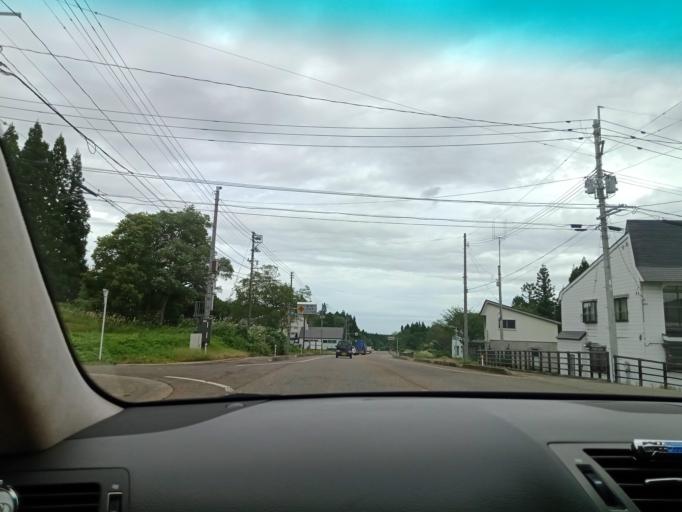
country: JP
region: Niigata
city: Arai
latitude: 36.8877
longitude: 138.2056
